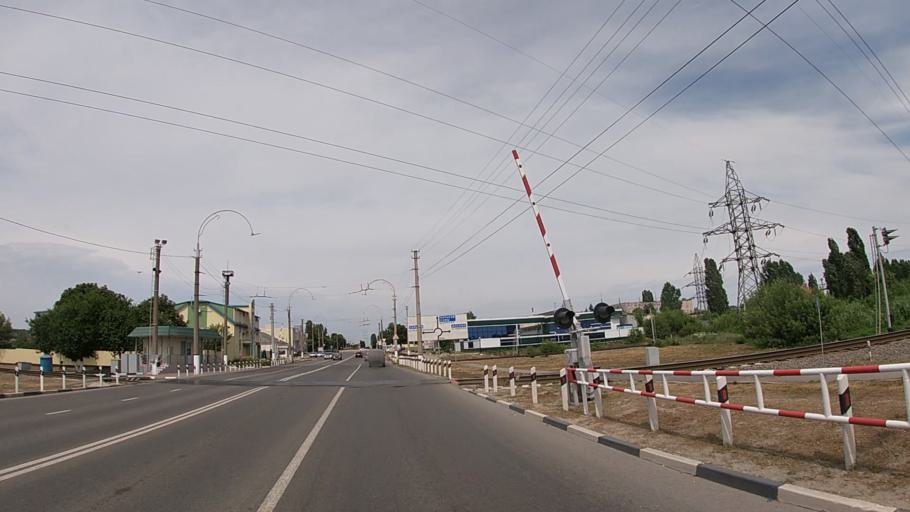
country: RU
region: Belgorod
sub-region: Belgorodskiy Rayon
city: Belgorod
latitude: 50.6121
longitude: 36.5383
